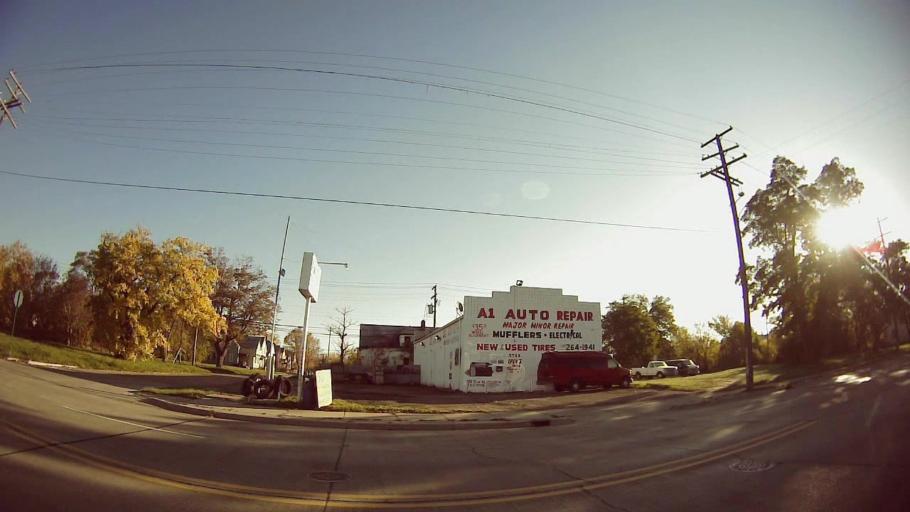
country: US
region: Michigan
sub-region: Wayne County
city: Hamtramck
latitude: 42.3825
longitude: -83.0175
